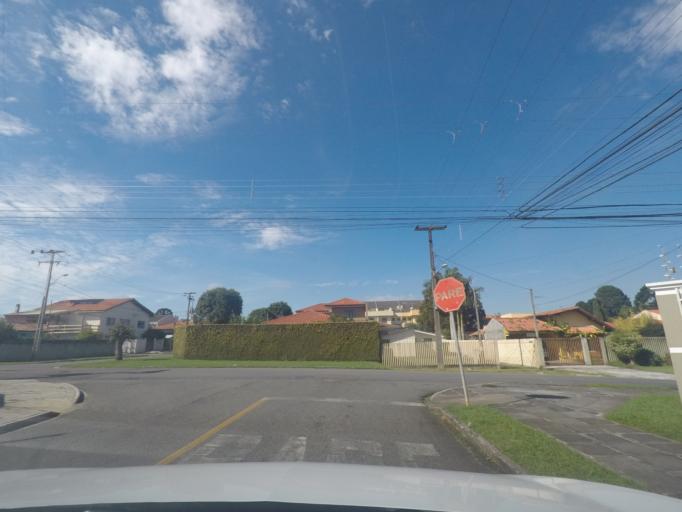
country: BR
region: Parana
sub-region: Sao Jose Dos Pinhais
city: Sao Jose dos Pinhais
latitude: -25.5064
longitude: -49.2574
